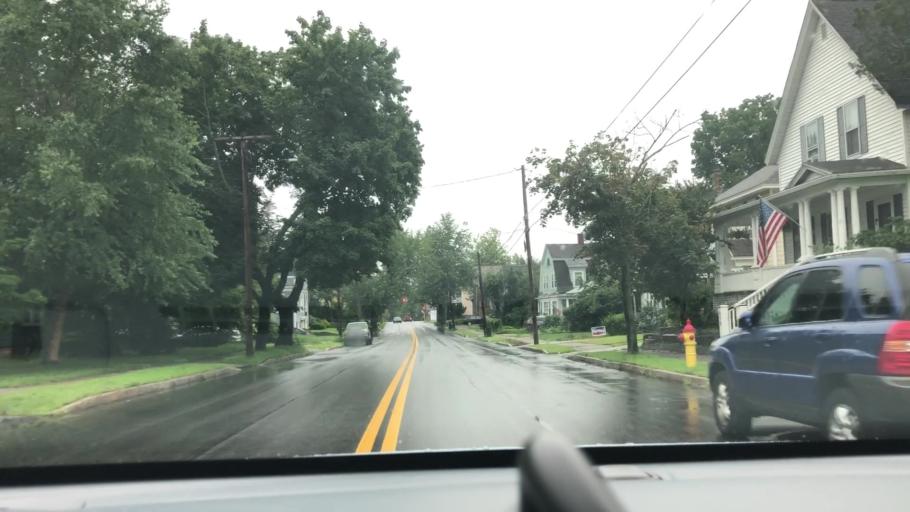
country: US
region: New Hampshire
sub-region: Hillsborough County
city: Manchester
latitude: 43.0090
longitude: -71.4605
